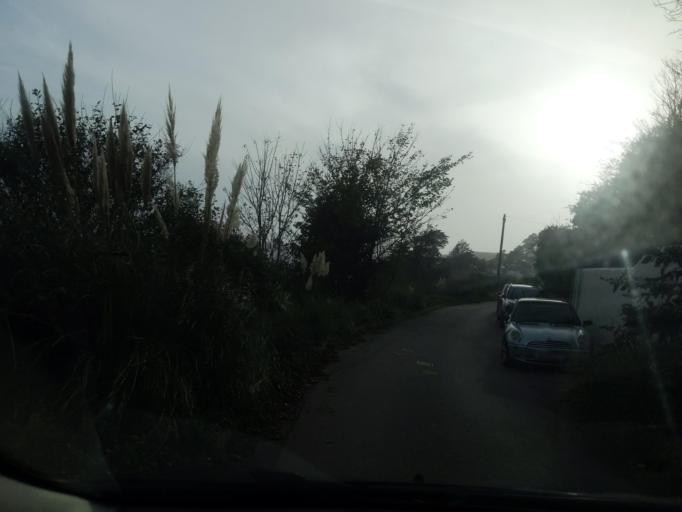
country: GB
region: England
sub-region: Cornwall
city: Looe
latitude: 50.3605
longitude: -4.4399
